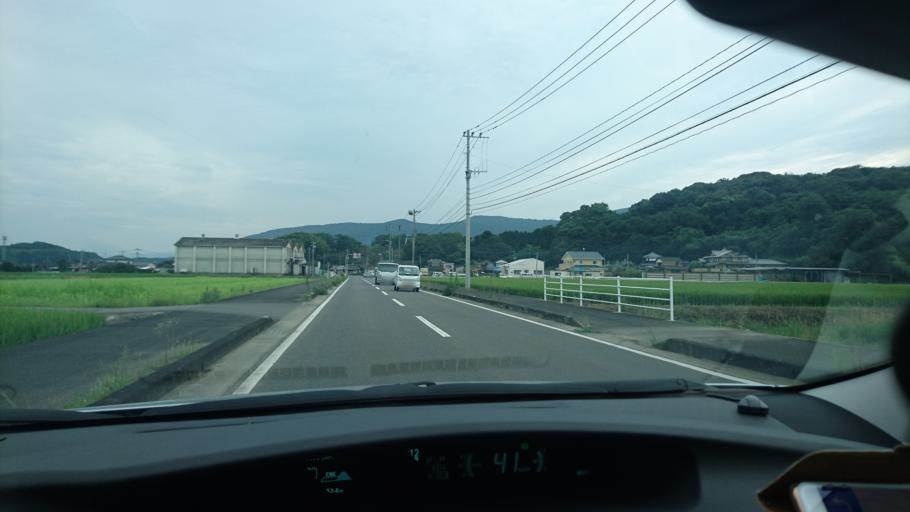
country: JP
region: Saga Prefecture
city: Takeocho-takeo
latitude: 33.1918
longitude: 130.1008
